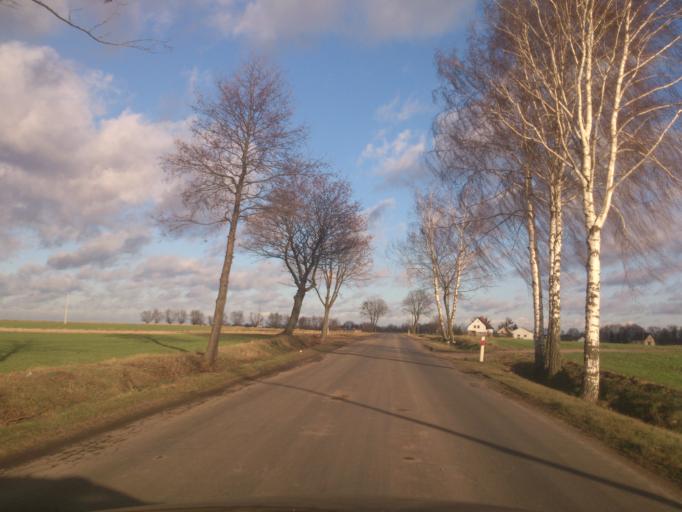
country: PL
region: Kujawsko-Pomorskie
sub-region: Powiat golubsko-dobrzynski
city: Ciechocin
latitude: 53.0389
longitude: 18.8936
